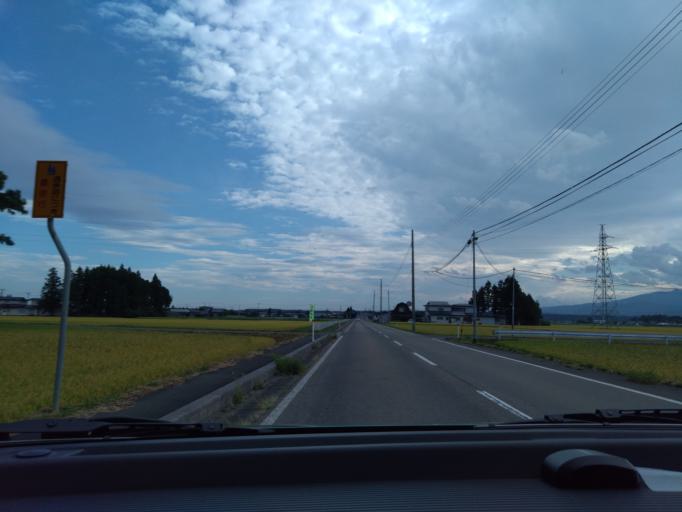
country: JP
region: Iwate
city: Kitakami
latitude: 39.3064
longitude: 141.0516
